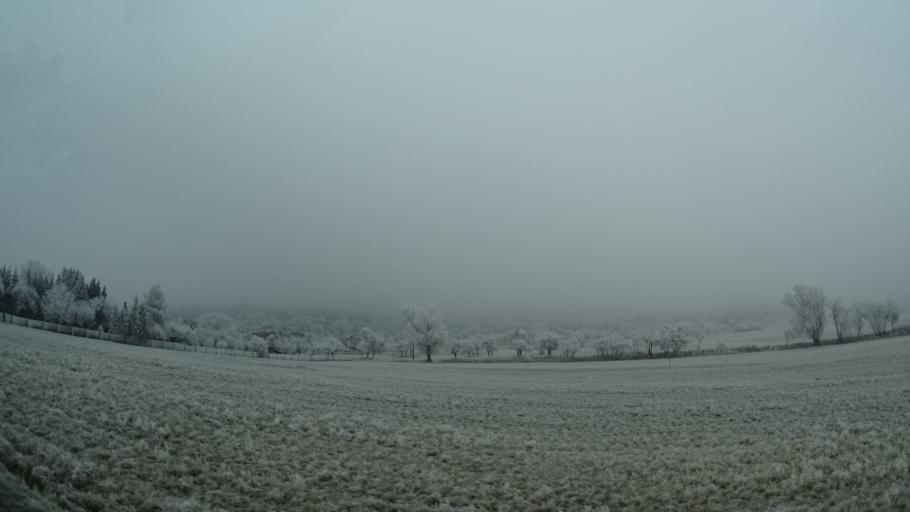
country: DE
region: Bavaria
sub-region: Regierungsbezirk Unterfranken
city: Willmars
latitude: 50.5265
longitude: 10.2936
